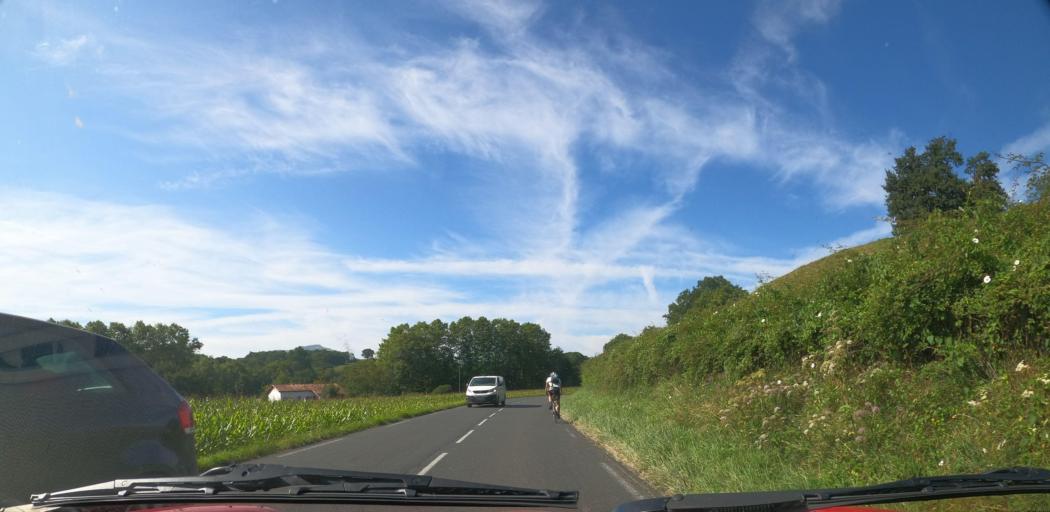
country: FR
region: Aquitaine
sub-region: Departement des Pyrenees-Atlantiques
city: Sare
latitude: 43.3135
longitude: -1.5634
